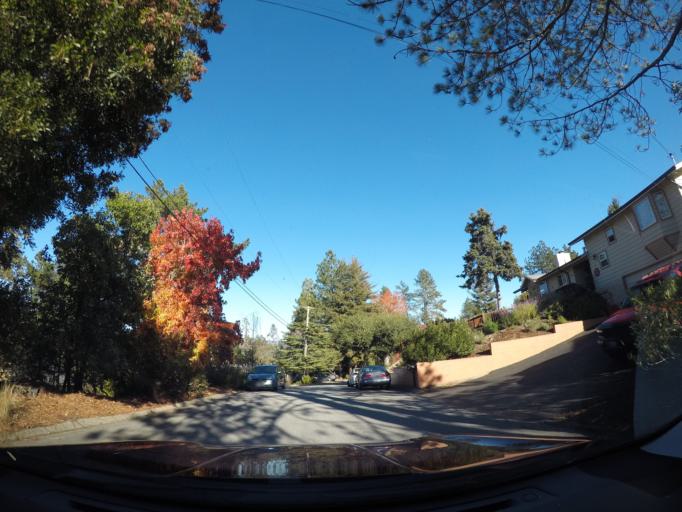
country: US
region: California
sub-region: Santa Cruz County
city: Mount Hermon
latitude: 37.0385
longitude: -122.0389
